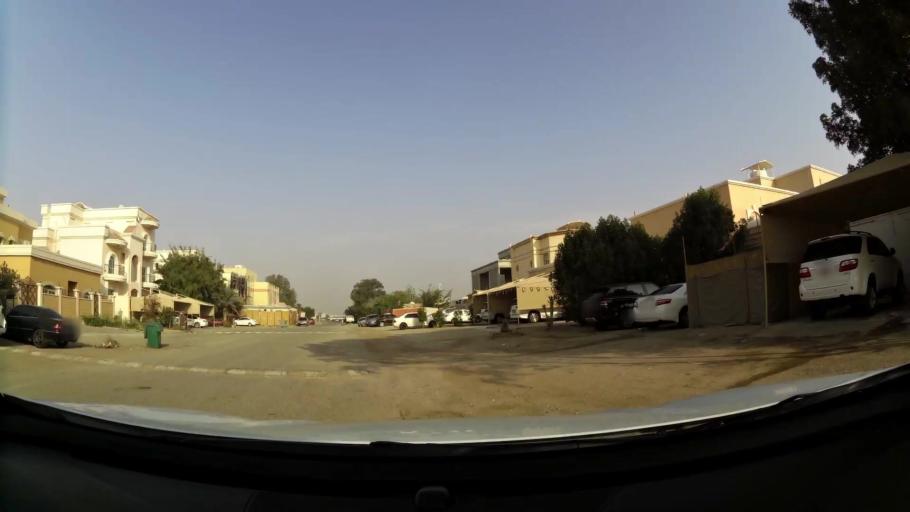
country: AE
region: Abu Dhabi
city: Abu Dhabi
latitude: 24.2927
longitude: 54.6292
